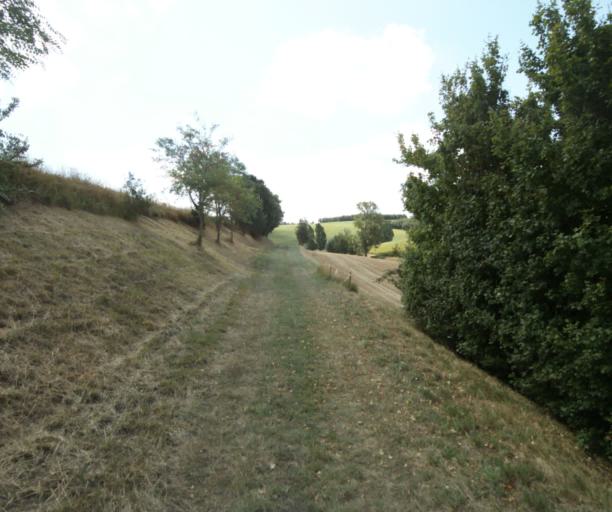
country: FR
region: Midi-Pyrenees
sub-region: Departement de la Haute-Garonne
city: Auriac-sur-Vendinelle
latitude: 43.4608
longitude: 1.7950
